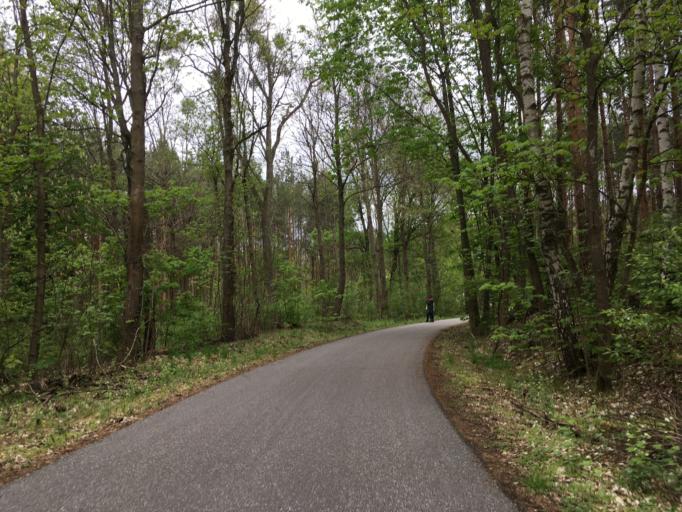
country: DE
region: Brandenburg
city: Bernau bei Berlin
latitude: 52.6953
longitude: 13.5411
